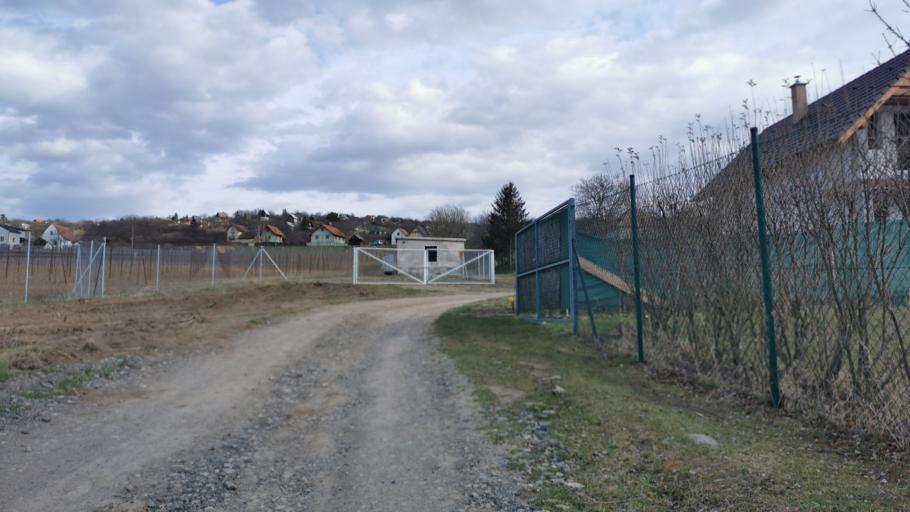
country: SK
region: Trnavsky
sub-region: Okres Skalica
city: Skalica
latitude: 48.8177
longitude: 17.2161
